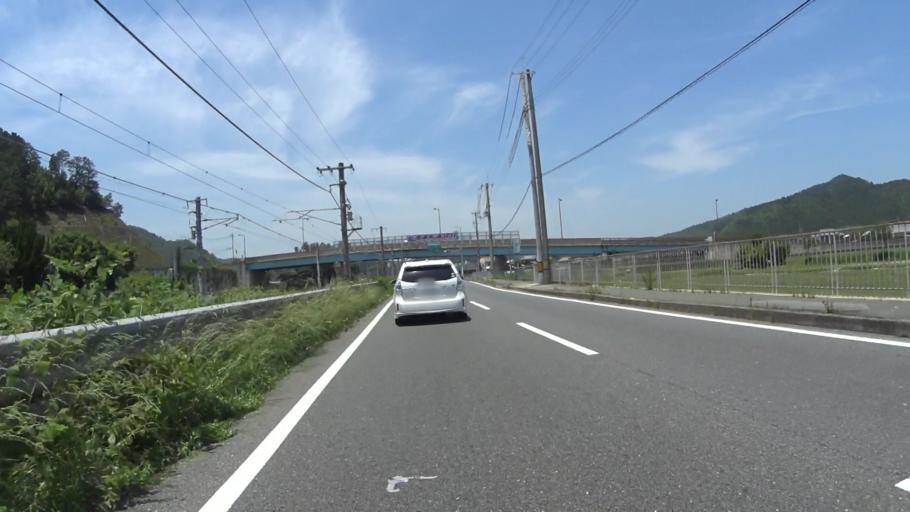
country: JP
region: Kyoto
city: Kameoka
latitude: 35.0734
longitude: 135.5260
